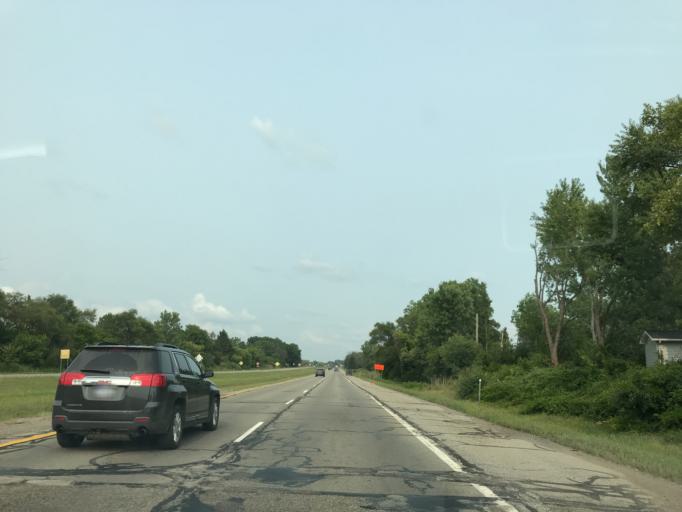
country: US
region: Michigan
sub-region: Ingham County
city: East Lansing
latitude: 42.7482
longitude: -84.4600
